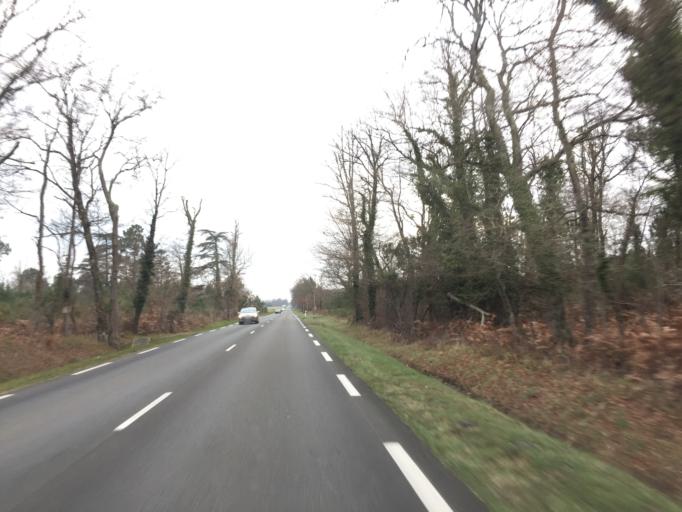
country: FR
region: Aquitaine
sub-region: Departement de la Gironde
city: Saint-Sauveur
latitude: 45.1939
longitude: -0.8538
